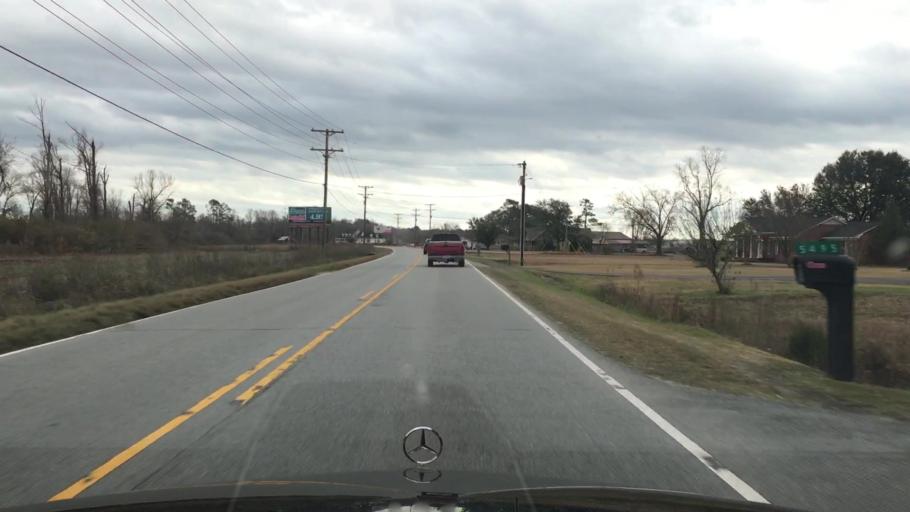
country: US
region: North Carolina
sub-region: Onslow County
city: Half Moon
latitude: 34.8487
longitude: -77.4811
